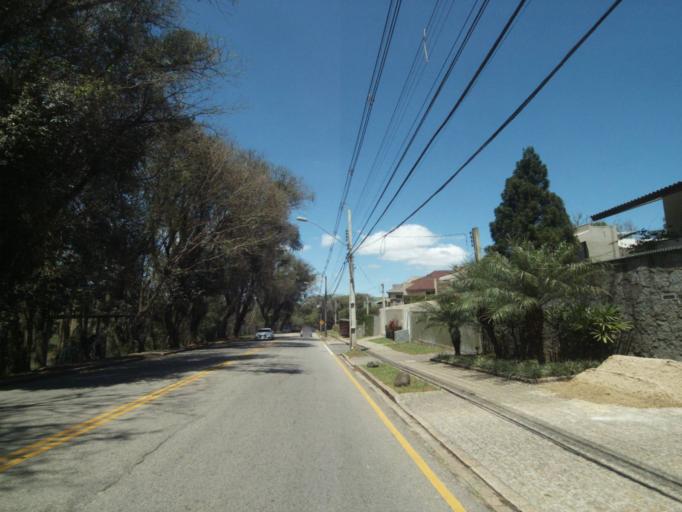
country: BR
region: Parana
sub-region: Curitiba
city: Curitiba
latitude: -25.3827
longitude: -49.2681
